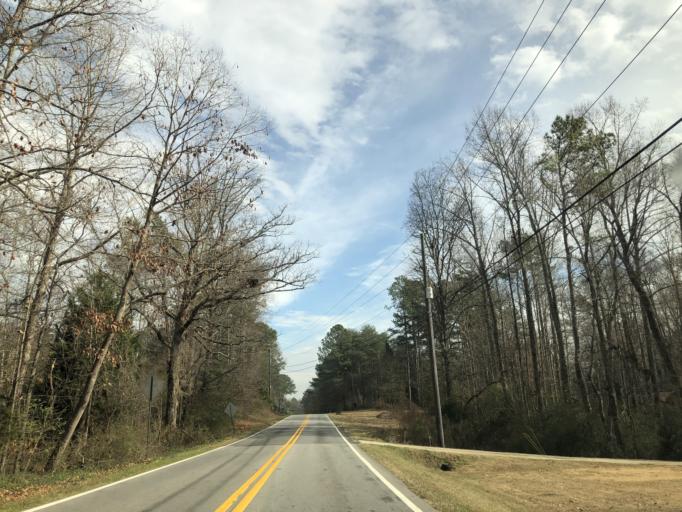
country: US
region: Georgia
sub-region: DeKalb County
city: Panthersville
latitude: 33.6428
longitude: -84.2034
